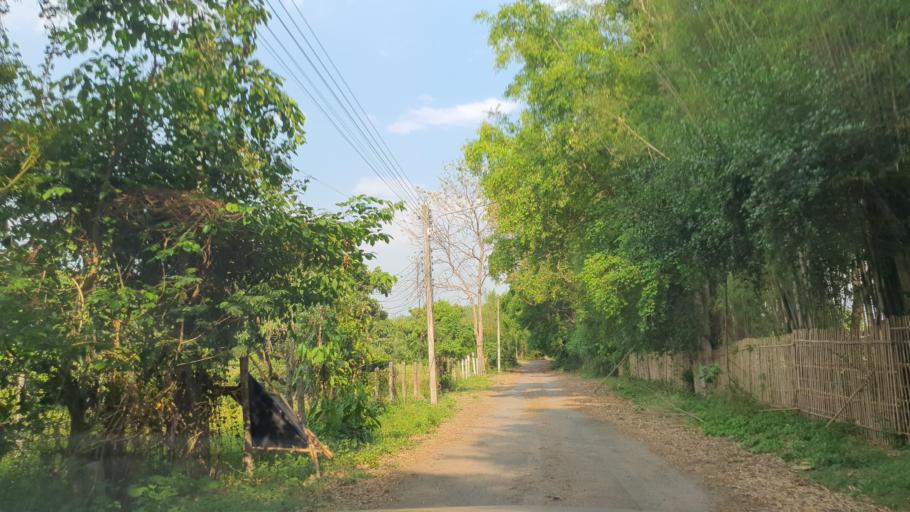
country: TH
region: Chiang Mai
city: Mae Wang
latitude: 18.6852
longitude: 98.8110
